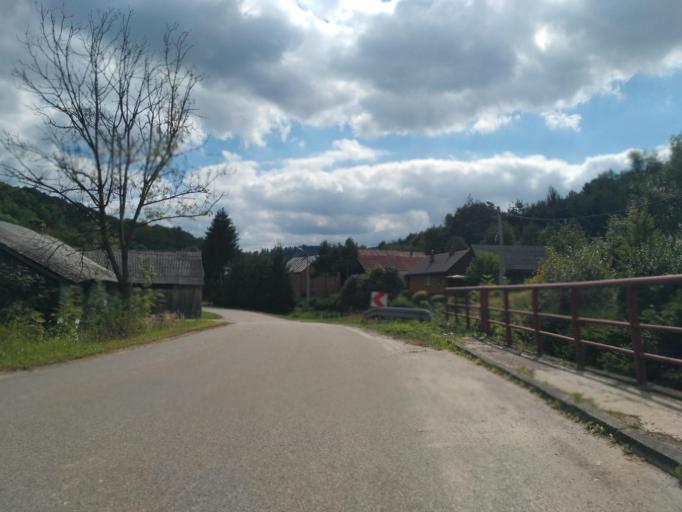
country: PL
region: Subcarpathian Voivodeship
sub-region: Powiat rzeszowski
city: Dynow
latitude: 49.7798
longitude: 22.2348
